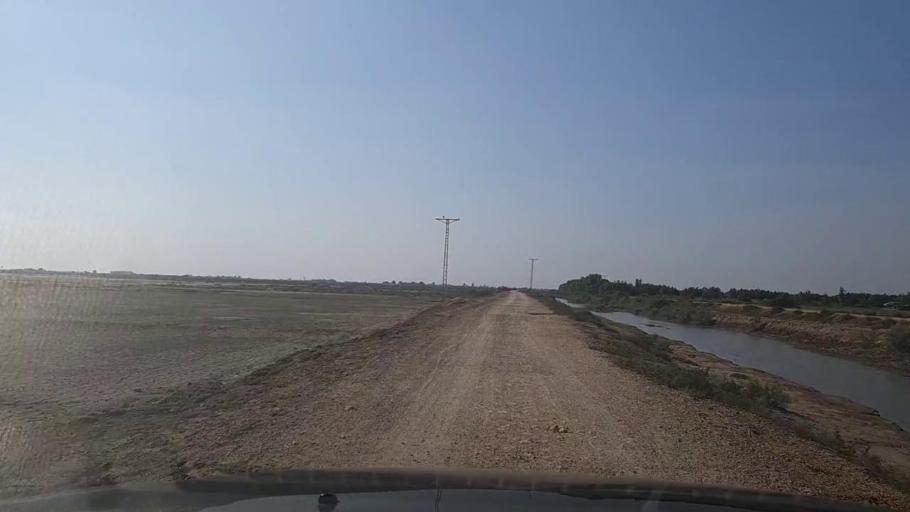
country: PK
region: Sindh
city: Thatta
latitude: 24.7111
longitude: 67.7660
